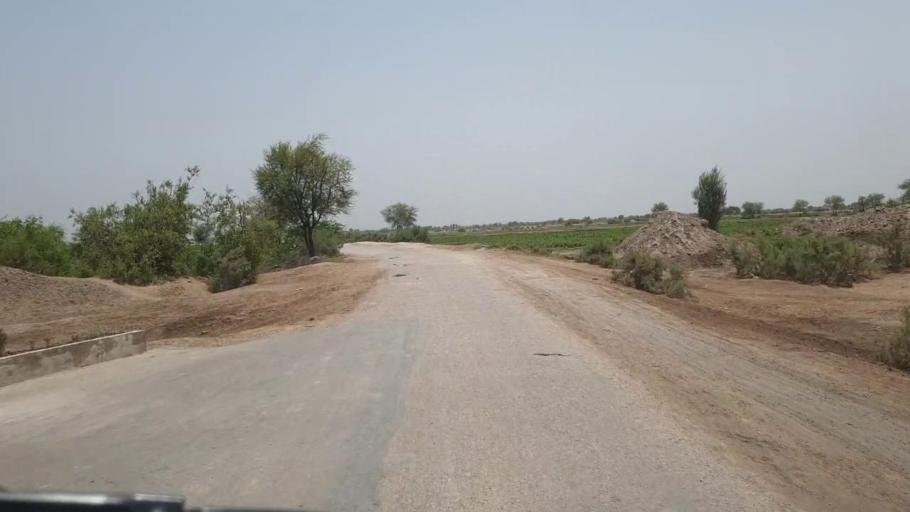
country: PK
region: Sindh
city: Daulatpur
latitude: 26.4608
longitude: 68.1193
